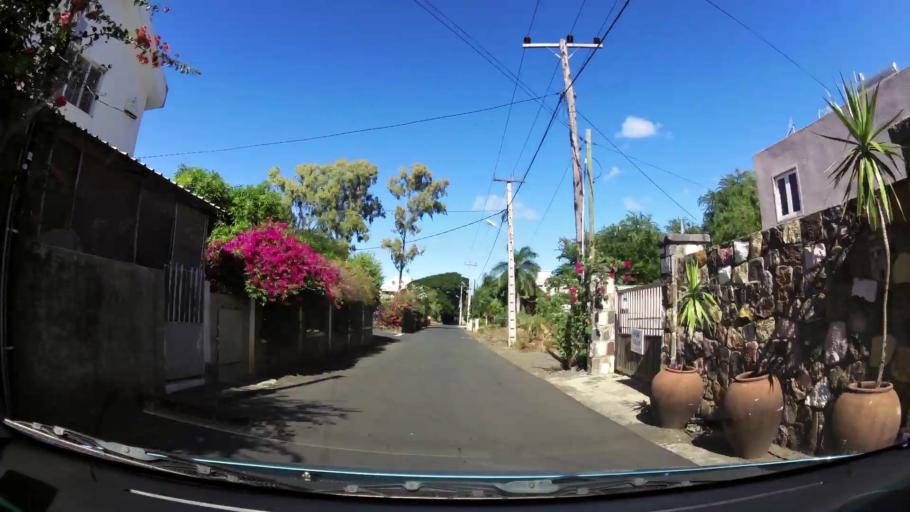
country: MU
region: Black River
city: Flic en Flac
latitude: -20.2744
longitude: 57.3724
